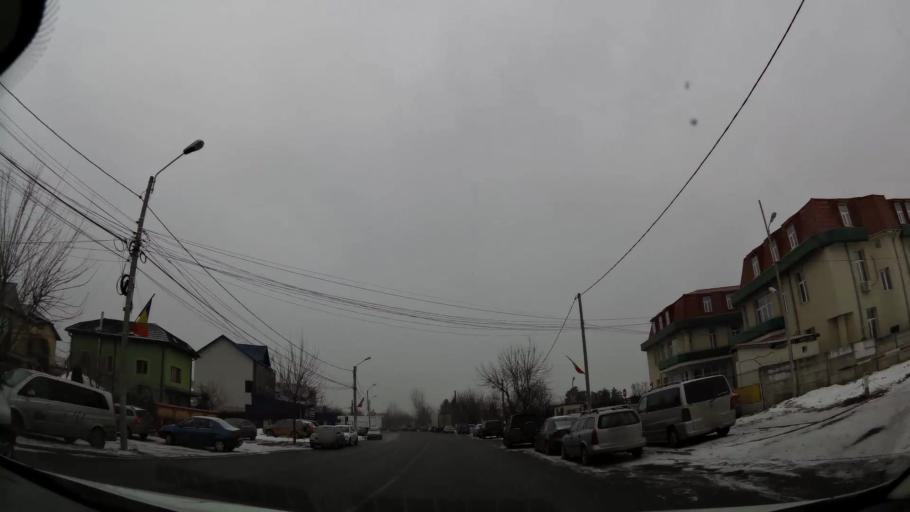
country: RO
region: Dambovita
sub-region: Municipiul Targoviste
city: Targoviste
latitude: 44.9343
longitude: 25.4396
